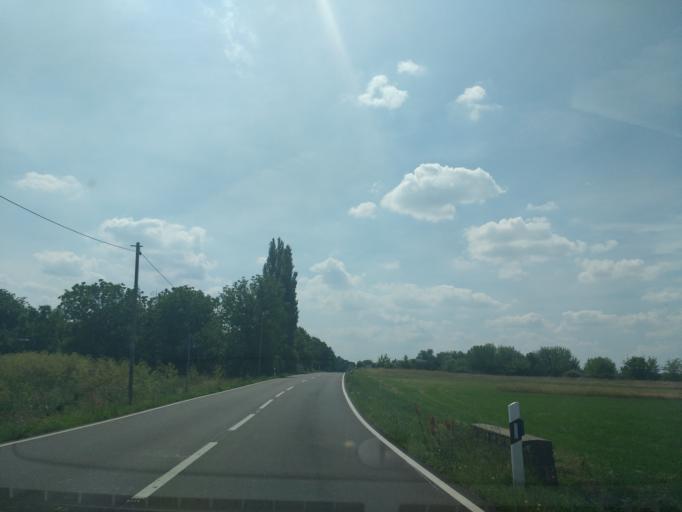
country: DE
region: Saxony-Anhalt
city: Dolbau
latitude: 51.4585
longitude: 12.0473
